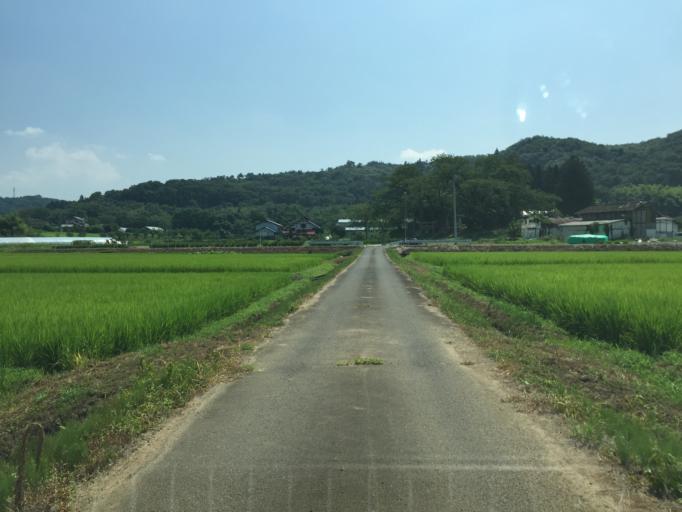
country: JP
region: Fukushima
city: Fukushima-shi
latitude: 37.7022
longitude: 140.4460
